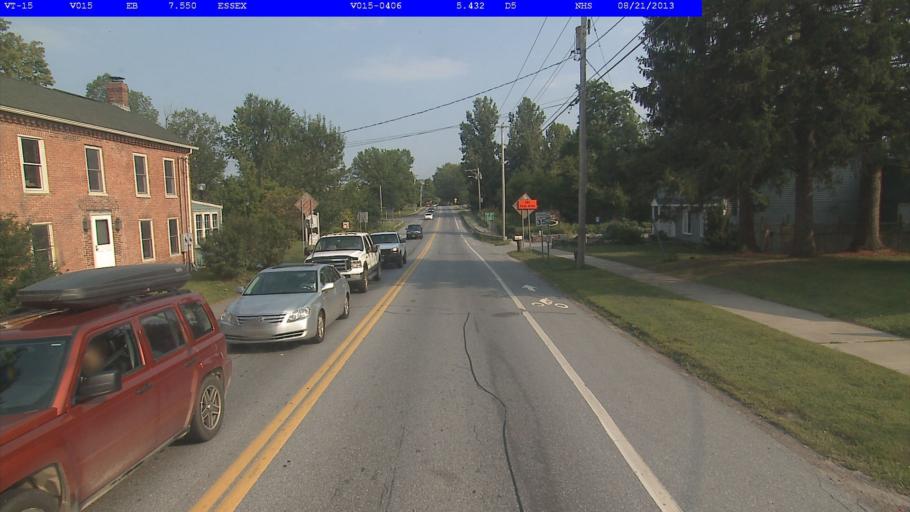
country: US
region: Vermont
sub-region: Chittenden County
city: Essex Junction
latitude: 44.5111
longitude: -73.0584
